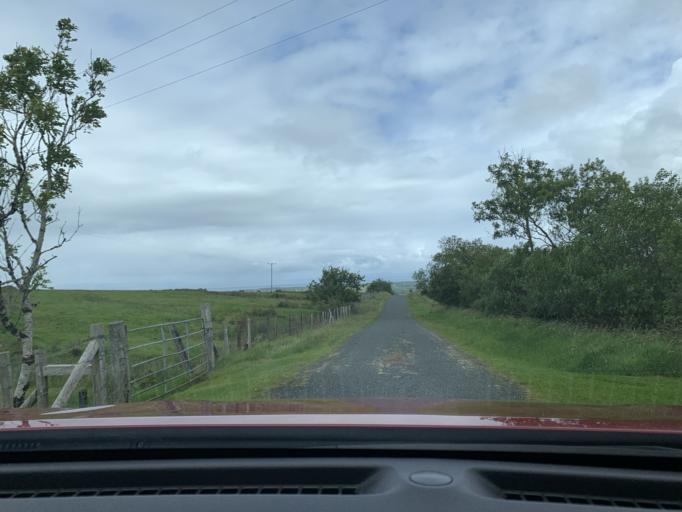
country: IE
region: Connaught
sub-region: County Leitrim
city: Kinlough
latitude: 54.3923
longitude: -8.4047
